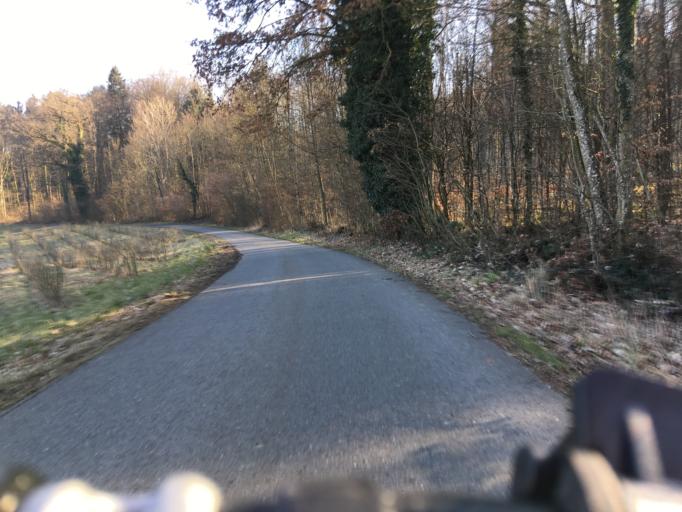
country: CH
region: Schaffhausen
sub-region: Bezirk Stein
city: Ramsen
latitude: 47.7229
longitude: 8.8034
